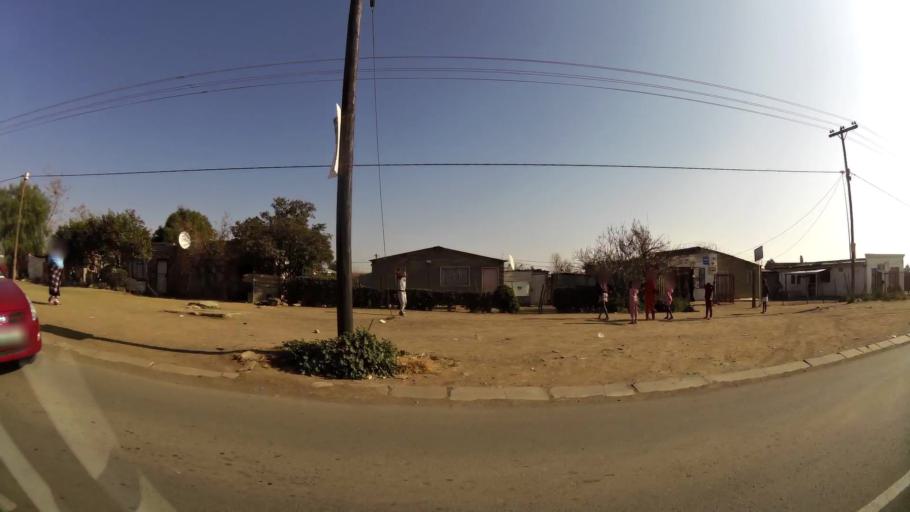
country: ZA
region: Orange Free State
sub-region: Mangaung Metropolitan Municipality
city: Bloemfontein
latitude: -29.1721
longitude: 26.2308
